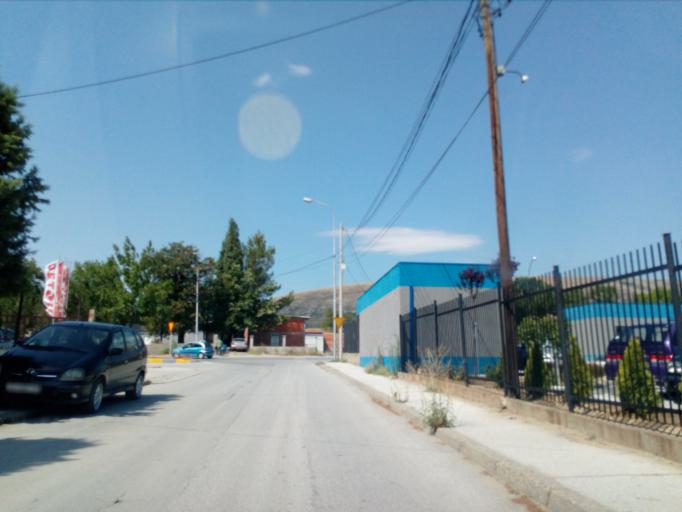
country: MK
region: Veles
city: Veles
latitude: 41.7225
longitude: 21.7655
